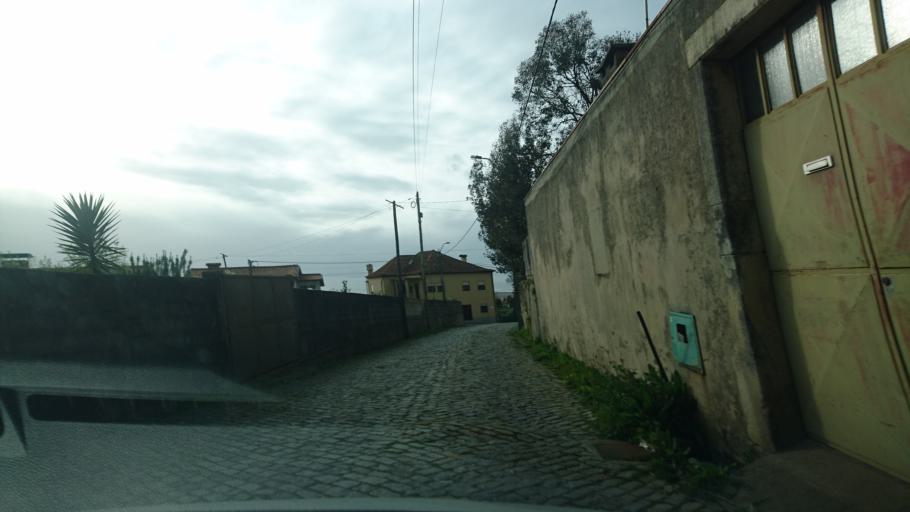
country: PT
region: Aveiro
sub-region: Ovar
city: Esmoriz
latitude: 40.9581
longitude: -8.6215
